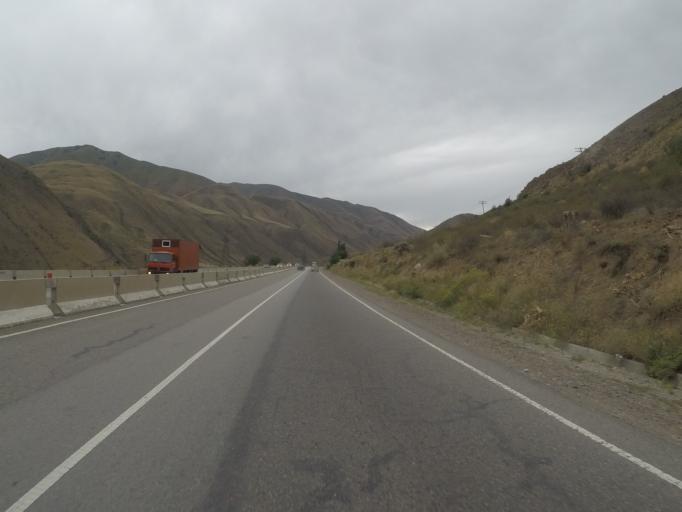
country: KG
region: Chuy
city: Bystrovka
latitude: 42.6661
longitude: 75.8896
